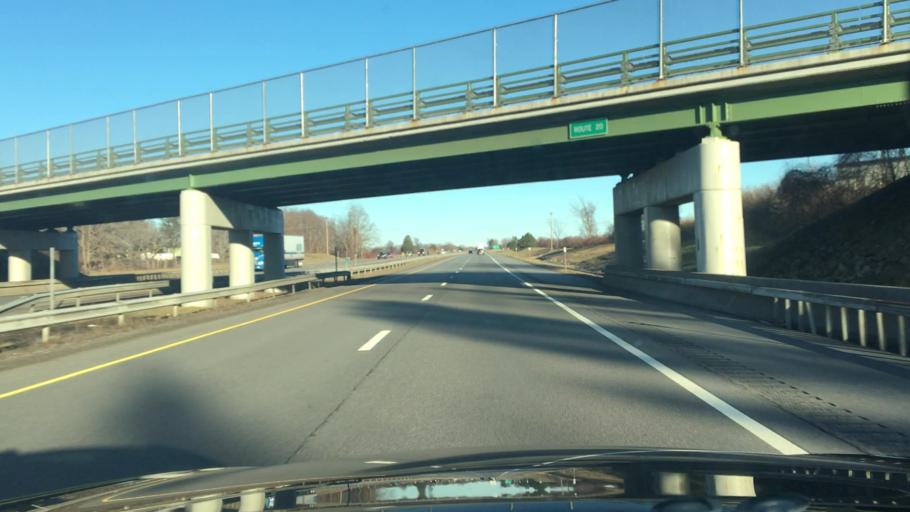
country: US
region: New York
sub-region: Chautauqua County
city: Silver Creek
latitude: 42.5124
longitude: -79.1895
